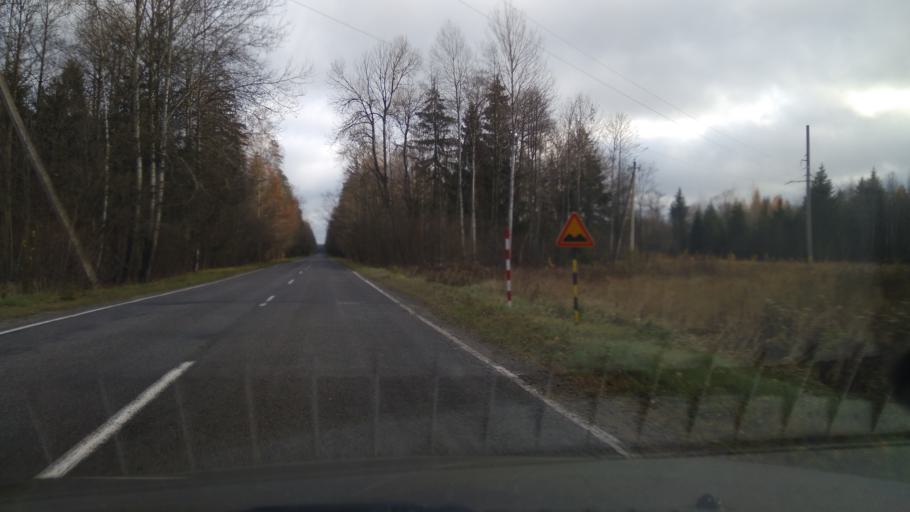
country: BY
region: Minsk
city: Slutsk
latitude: 53.2069
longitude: 27.7735
